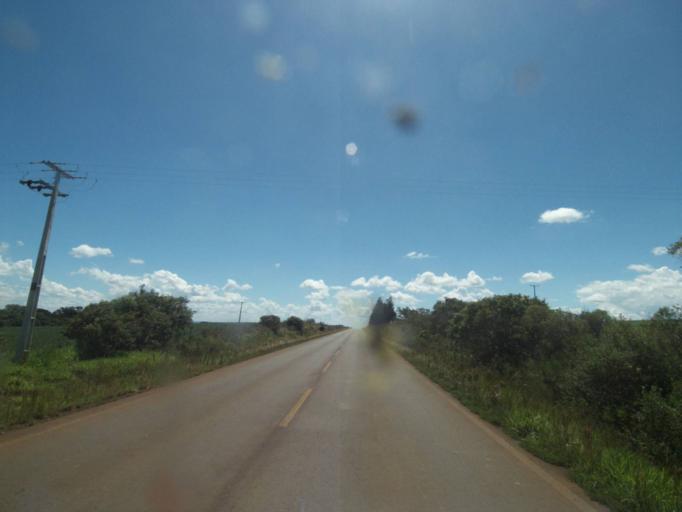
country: BR
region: Parana
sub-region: Pinhao
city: Pinhao
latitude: -25.8132
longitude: -52.0506
